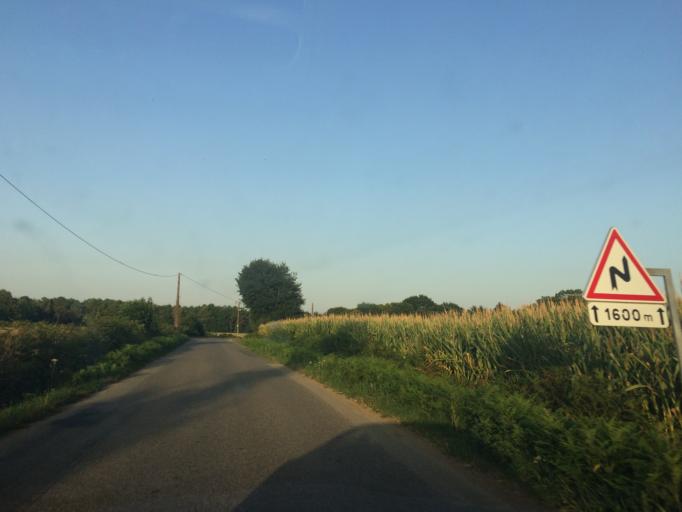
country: FR
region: Brittany
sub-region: Departement du Morbihan
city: Allaire
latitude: 47.6360
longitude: -2.2108
